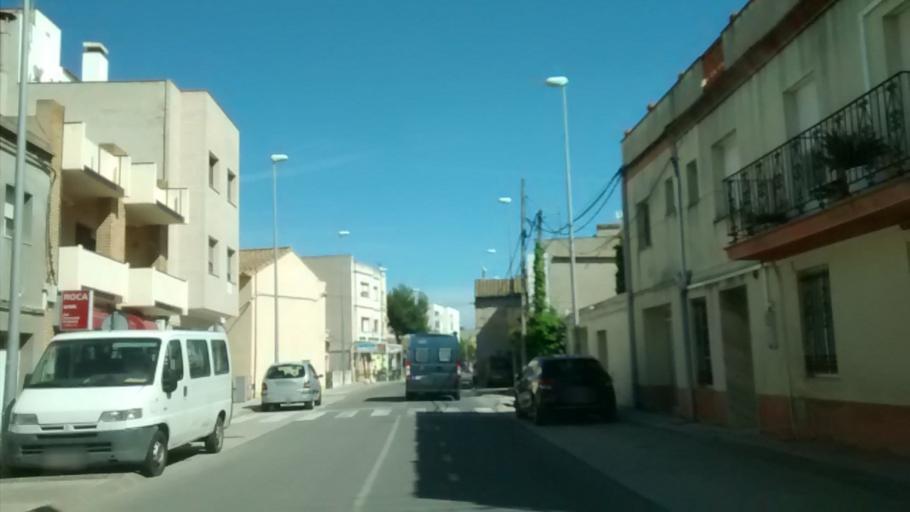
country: ES
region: Catalonia
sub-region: Provincia de Tarragona
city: Deltebre
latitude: 40.7161
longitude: 0.7433
